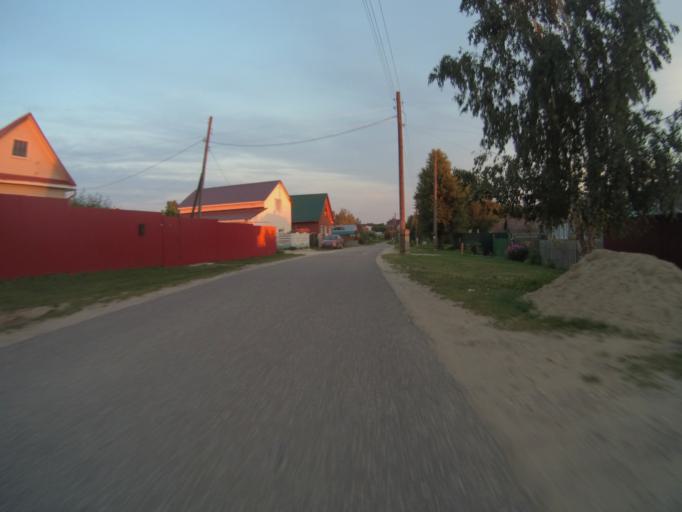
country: RU
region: Vladimir
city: Kommunar
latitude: 56.0782
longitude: 40.4921
